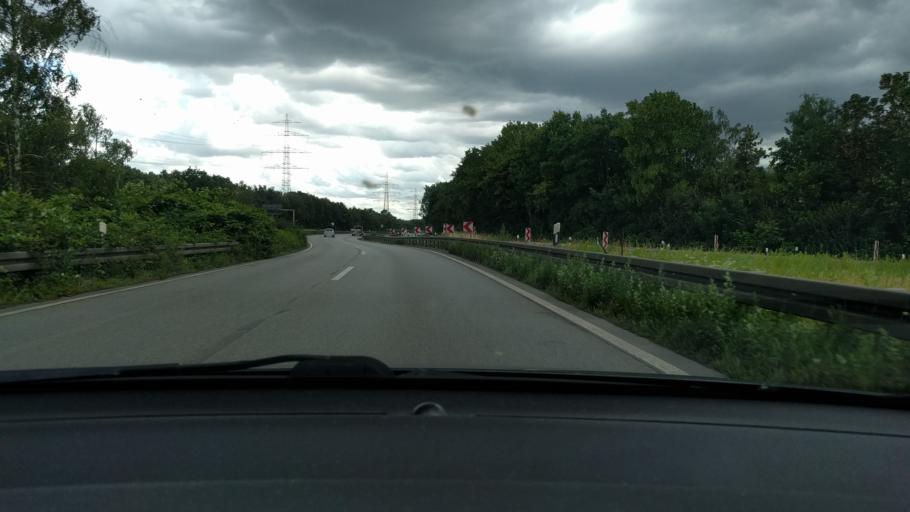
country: DE
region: North Rhine-Westphalia
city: Waltrop
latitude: 51.5845
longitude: 7.3667
